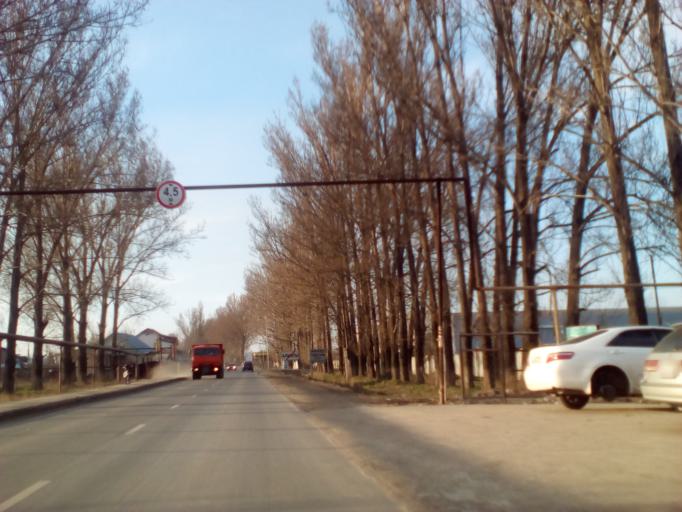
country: KZ
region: Almaty Oblysy
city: Burunday
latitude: 43.2505
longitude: 76.7840
